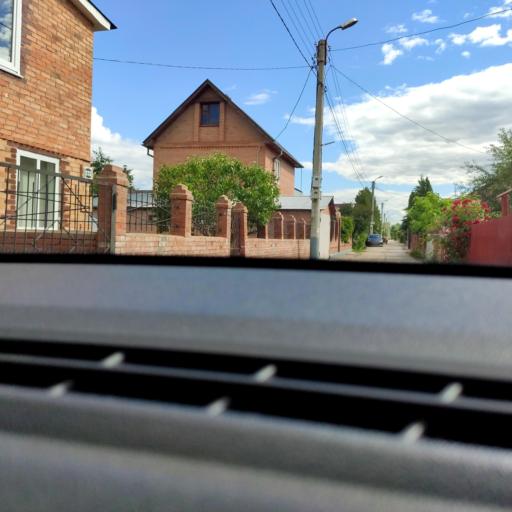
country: RU
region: Samara
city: Podstepki
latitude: 53.5849
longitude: 49.0684
